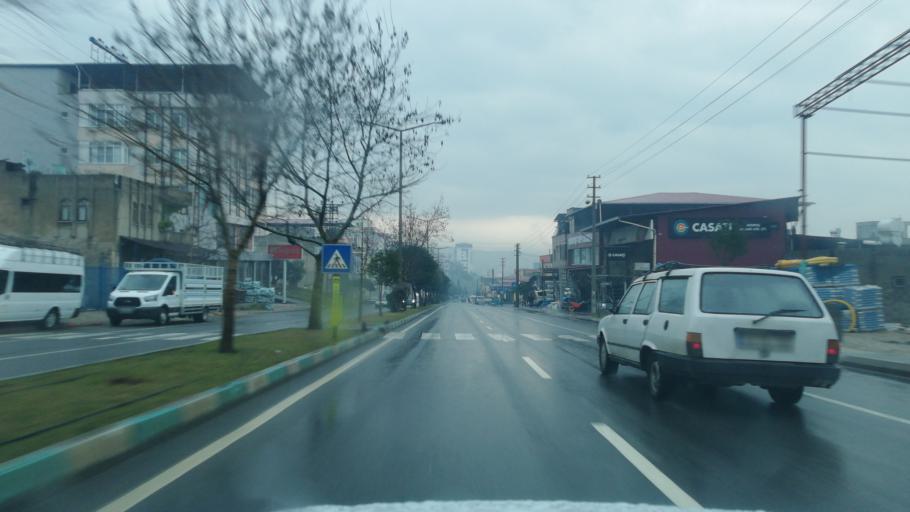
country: TR
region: Kahramanmaras
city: Kahramanmaras
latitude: 37.5824
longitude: 36.9522
